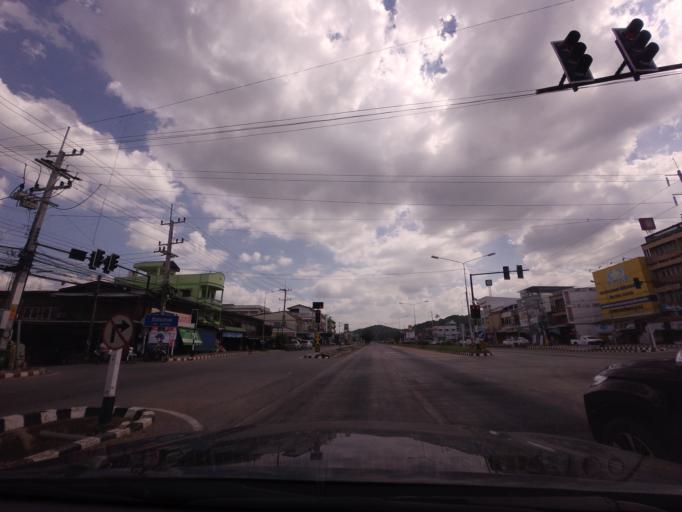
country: TH
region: Phetchabun
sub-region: Amphoe Bueng Sam Phan
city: Bueng Sam Phan
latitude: 15.7805
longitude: 101.0063
